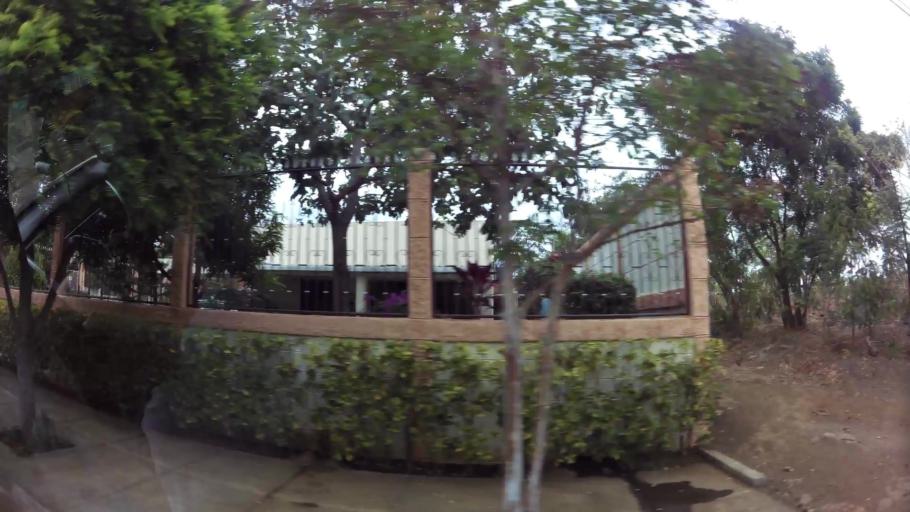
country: NI
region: Masaya
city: Ticuantepe
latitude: 12.0534
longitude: -86.1921
